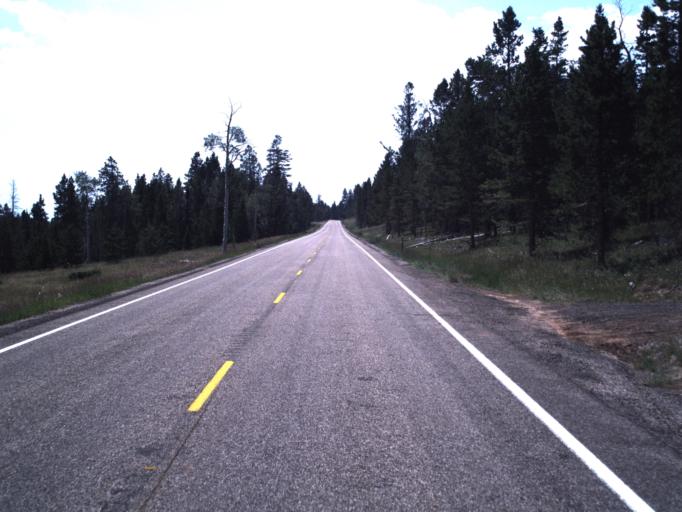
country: US
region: Utah
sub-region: Uintah County
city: Maeser
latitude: 40.7393
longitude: -109.4713
